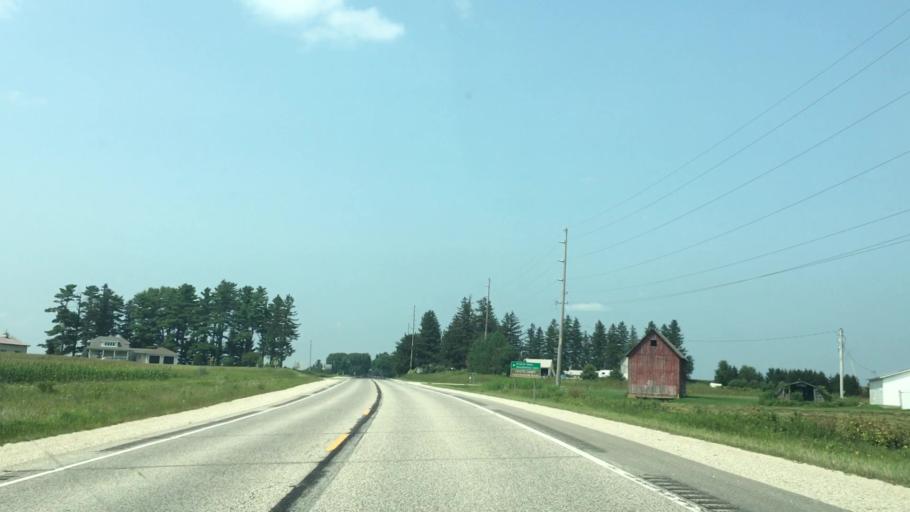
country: US
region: Iowa
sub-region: Fayette County
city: West Union
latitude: 42.9049
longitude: -91.8112
